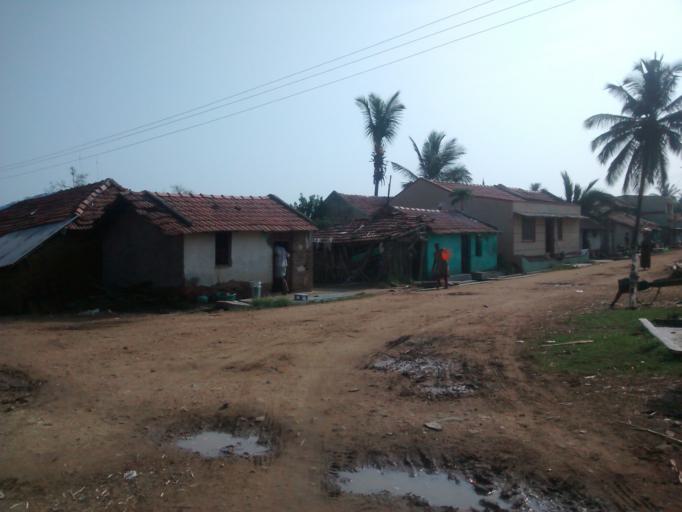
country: IN
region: Karnataka
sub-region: Hassan
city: Hassan
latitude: 12.9321
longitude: 76.1588
